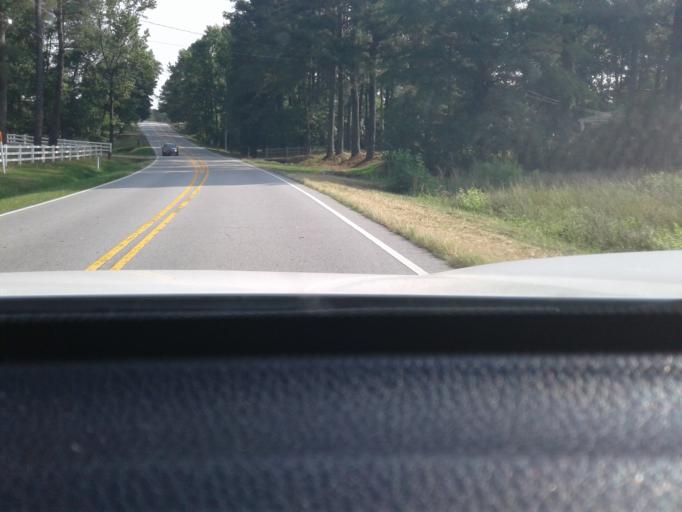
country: US
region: North Carolina
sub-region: Johnston County
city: Benson
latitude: 35.4005
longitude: -78.5419
